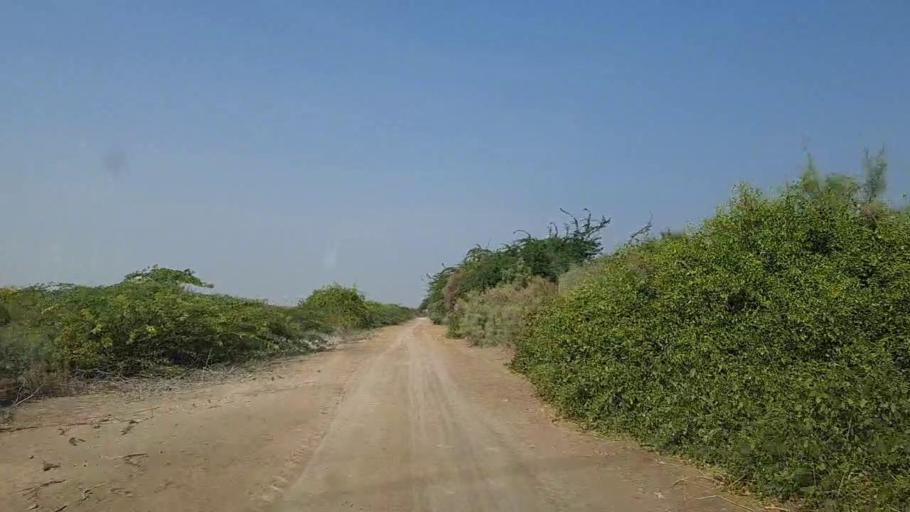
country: PK
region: Sindh
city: Mirpur Sakro
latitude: 24.5513
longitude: 67.5566
